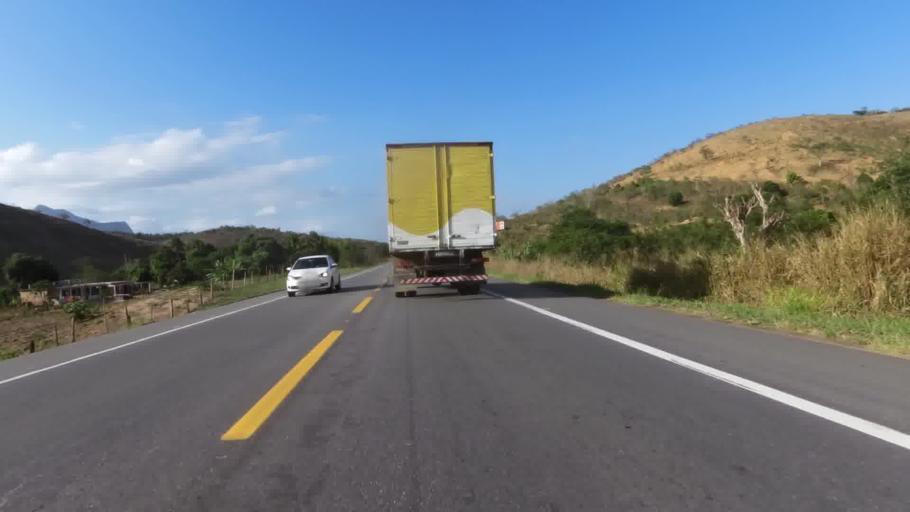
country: BR
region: Espirito Santo
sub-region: Mimoso Do Sul
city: Mimoso do Sul
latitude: -21.1714
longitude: -41.2919
